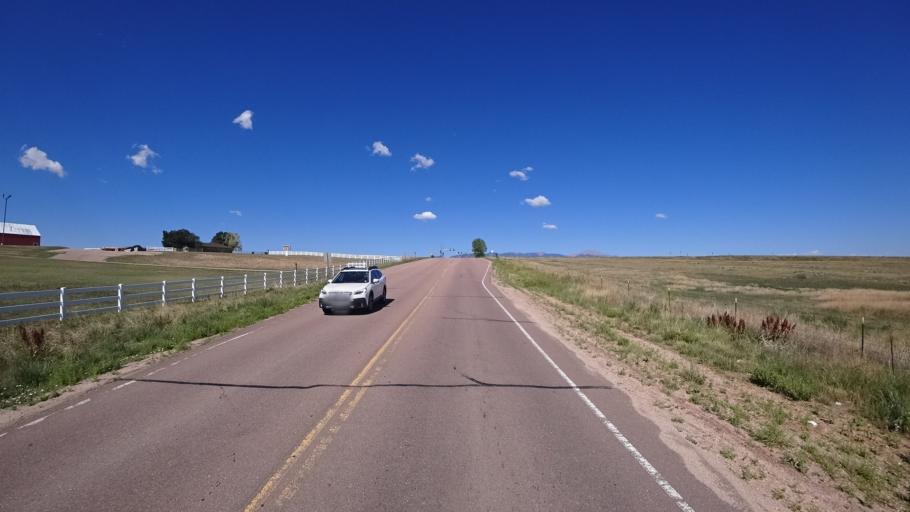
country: US
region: Colorado
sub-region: El Paso County
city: Security-Widefield
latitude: 38.7375
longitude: -104.6798
